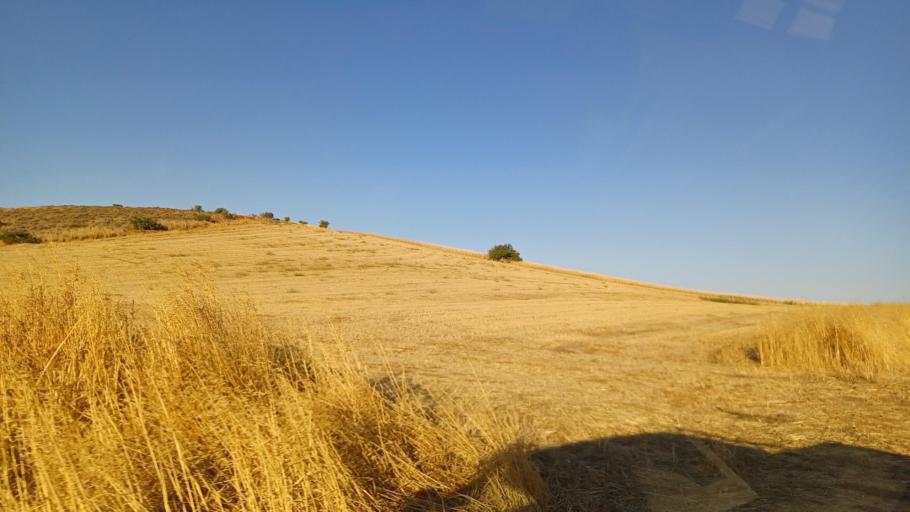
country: CY
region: Larnaka
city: Troulloi
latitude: 35.0301
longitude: 33.6460
